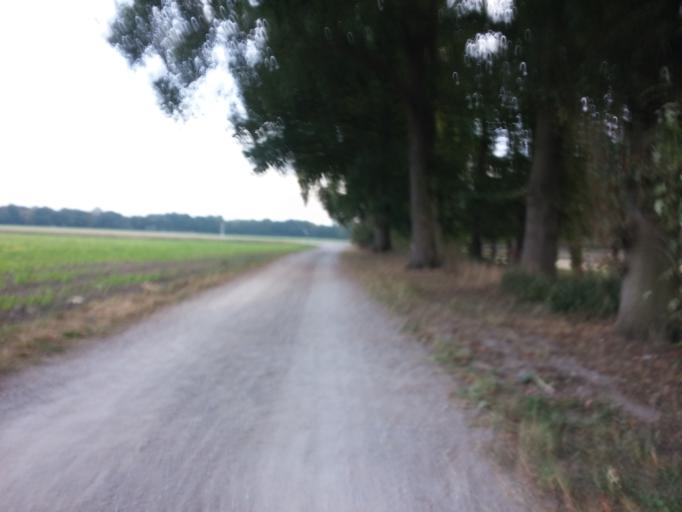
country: DE
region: North Rhine-Westphalia
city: Marl
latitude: 51.6132
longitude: 7.0442
